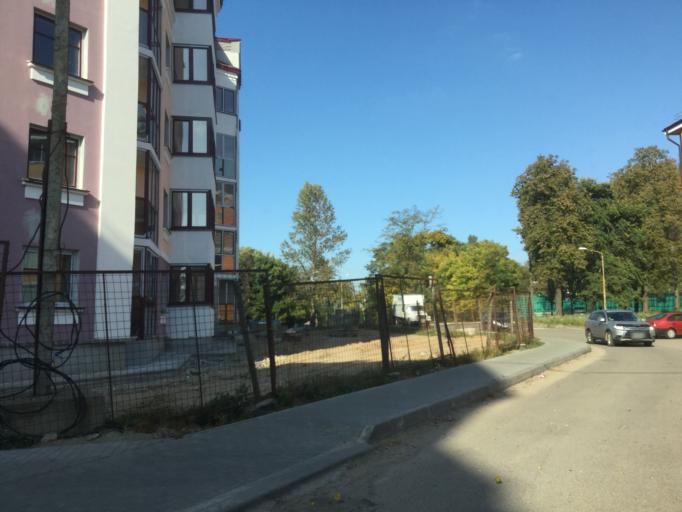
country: BY
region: Vitebsk
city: Vitebsk
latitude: 55.1727
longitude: 30.1949
